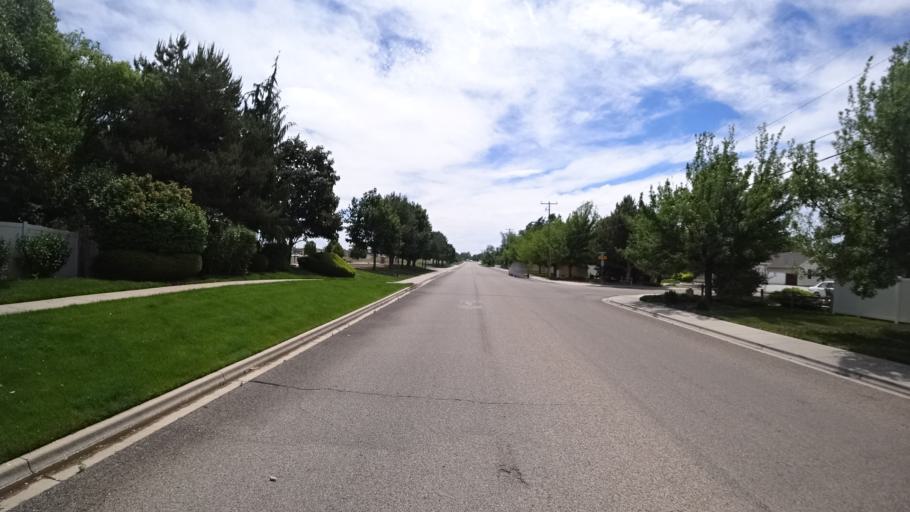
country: US
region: Idaho
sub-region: Ada County
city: Meridian
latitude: 43.6225
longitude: -116.3244
